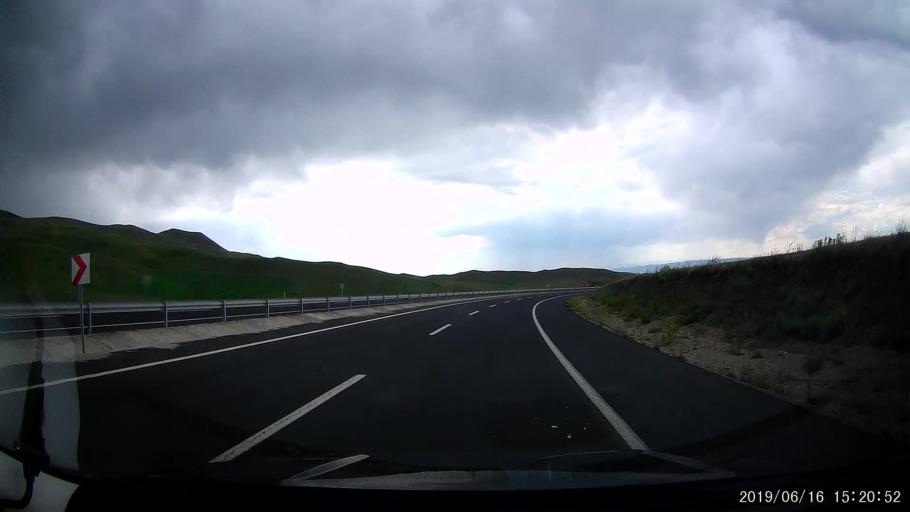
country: TR
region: Erzurum
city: Aras
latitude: 39.9729
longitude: 42.2547
